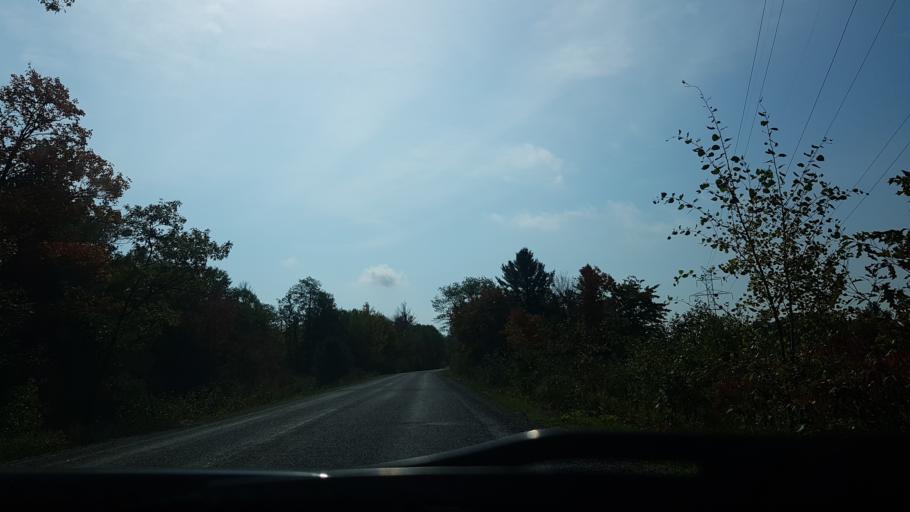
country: CA
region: Ontario
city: Gravenhurst
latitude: 44.8260
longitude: -79.2126
